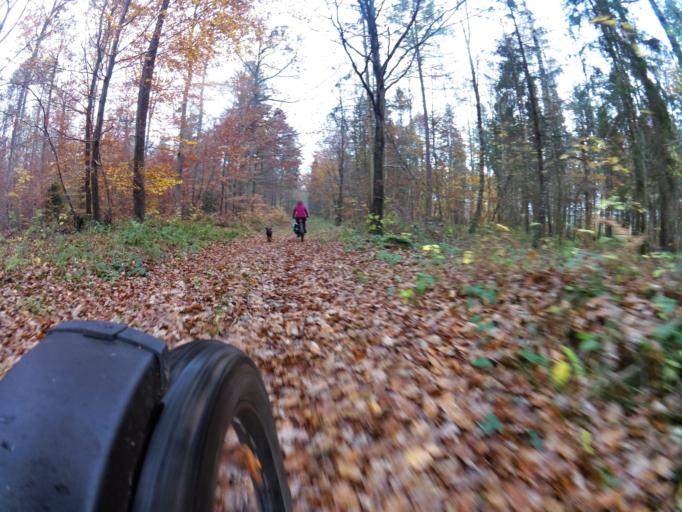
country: PL
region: Pomeranian Voivodeship
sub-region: Powiat pucki
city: Krokowa
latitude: 54.7354
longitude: 18.1306
